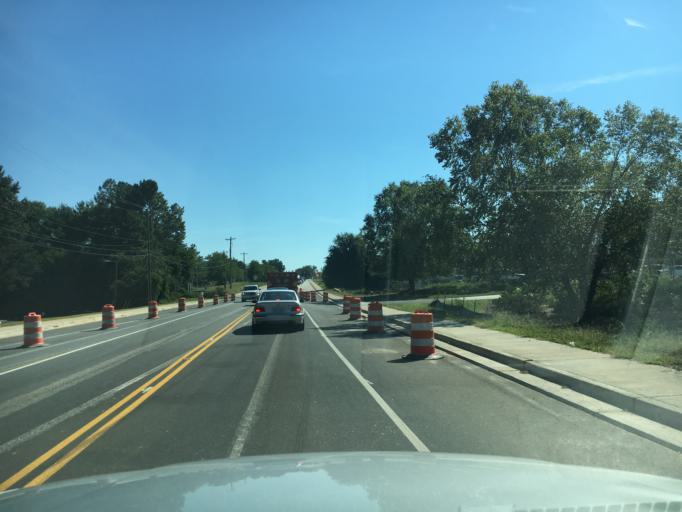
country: US
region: South Carolina
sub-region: Greenville County
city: Mauldin
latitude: 34.8370
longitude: -82.2852
